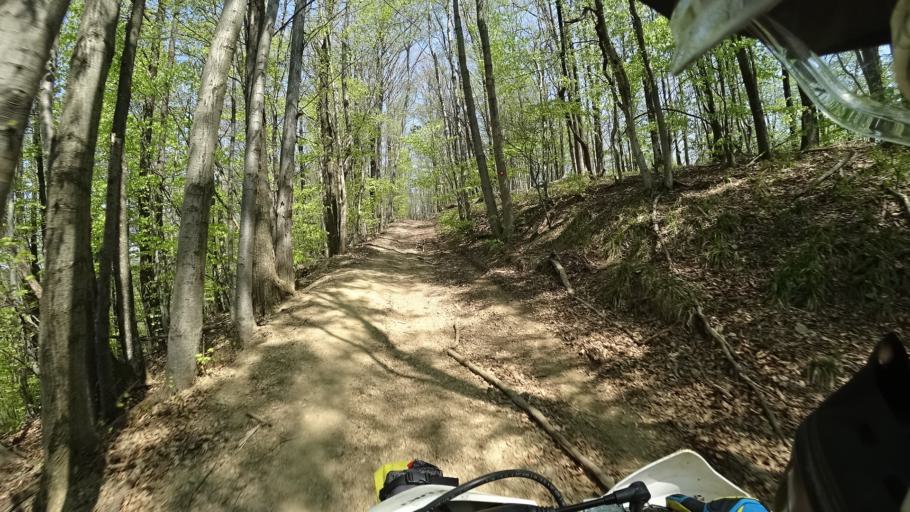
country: HR
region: Zagrebacka
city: Jablanovec
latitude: 45.8759
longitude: 15.9032
